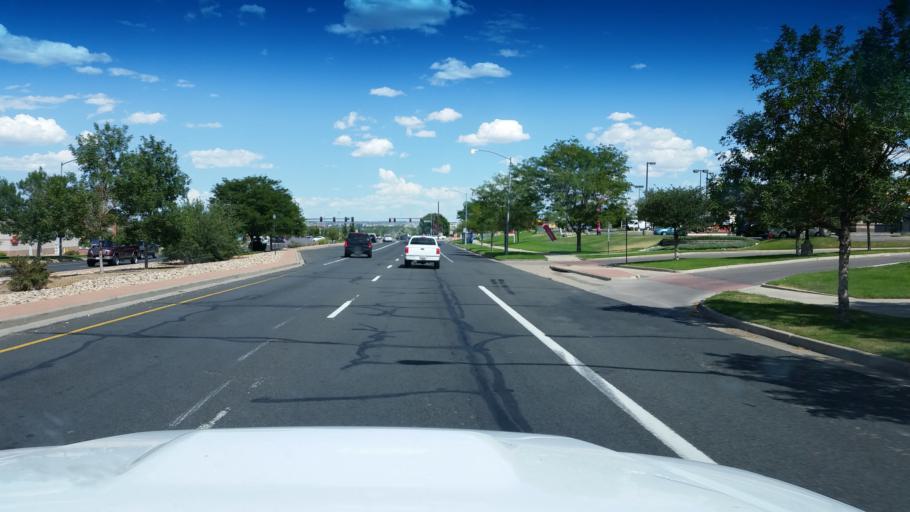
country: US
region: Colorado
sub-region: Adams County
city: Thornton
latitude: 39.8848
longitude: -104.9428
